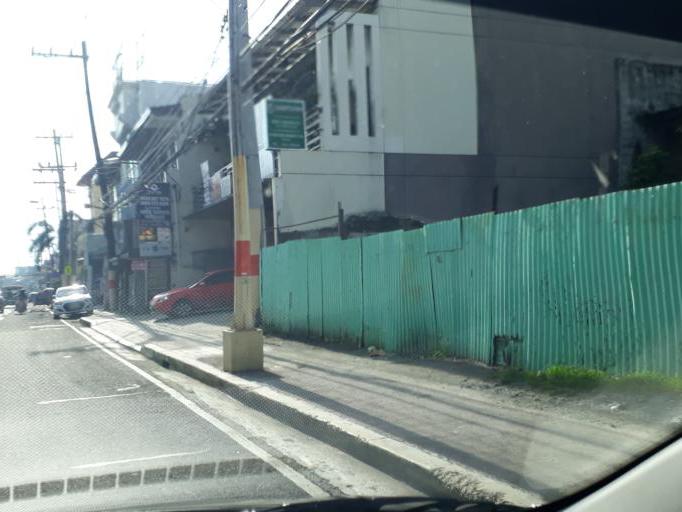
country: PH
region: Metro Manila
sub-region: Caloocan City
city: Niugan
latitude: 14.6516
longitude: 120.9815
